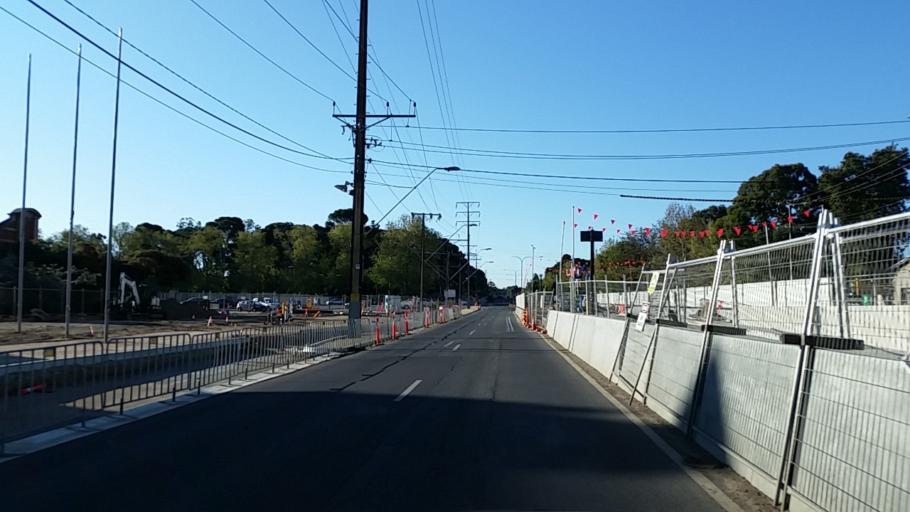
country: AU
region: South Australia
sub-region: Adelaide
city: Adelaide
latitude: -34.9177
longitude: 138.6146
